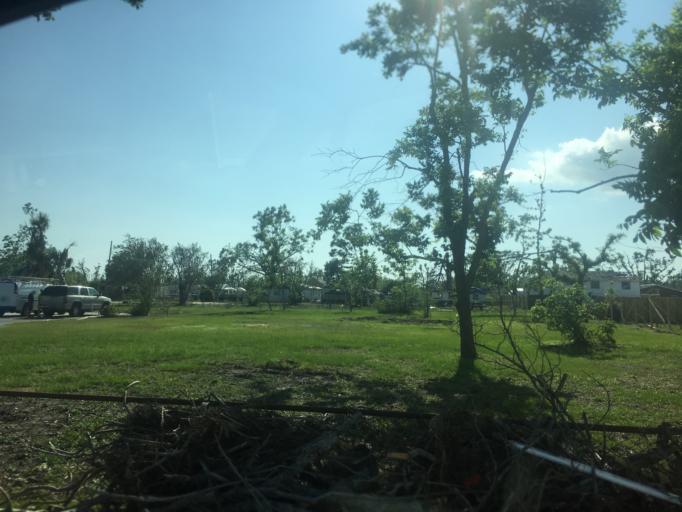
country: US
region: Florida
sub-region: Bay County
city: Springfield
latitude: 30.1588
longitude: -85.6208
